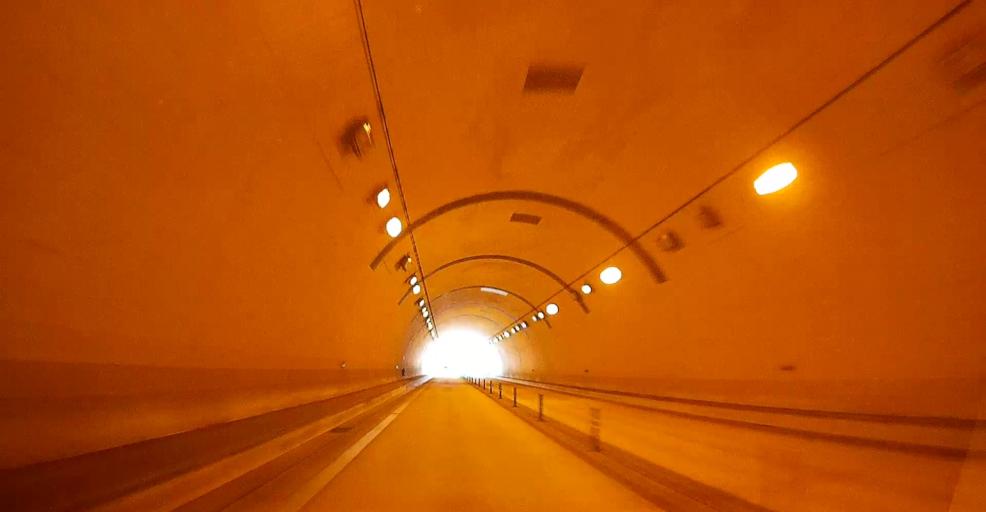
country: JP
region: Kumamoto
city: Yatsushiro
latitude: 32.5097
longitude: 130.4079
